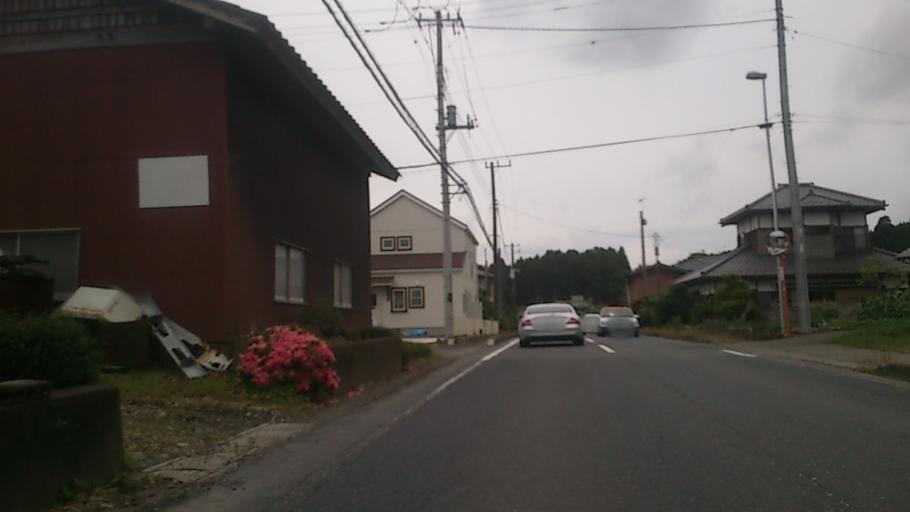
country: JP
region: Ibaraki
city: Okunoya
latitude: 36.2891
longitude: 140.3814
